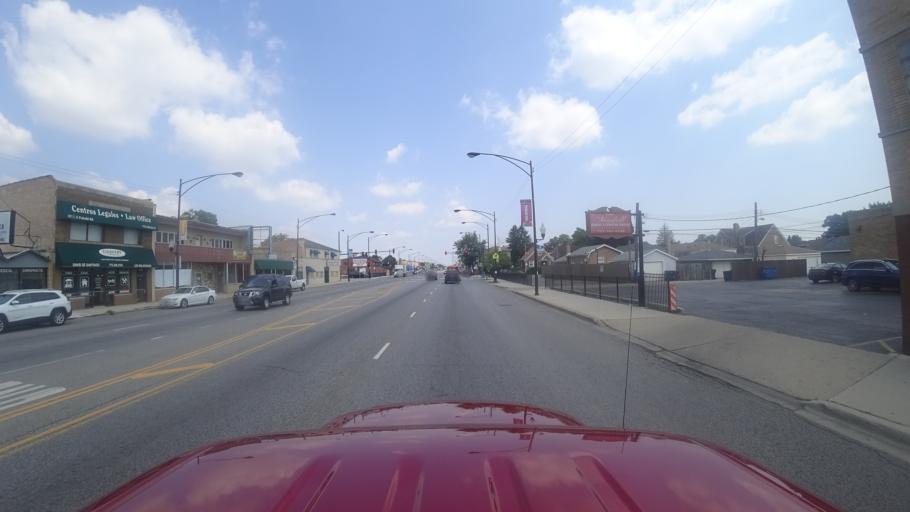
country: US
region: Illinois
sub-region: Cook County
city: Hometown
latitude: 41.7888
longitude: -87.7230
